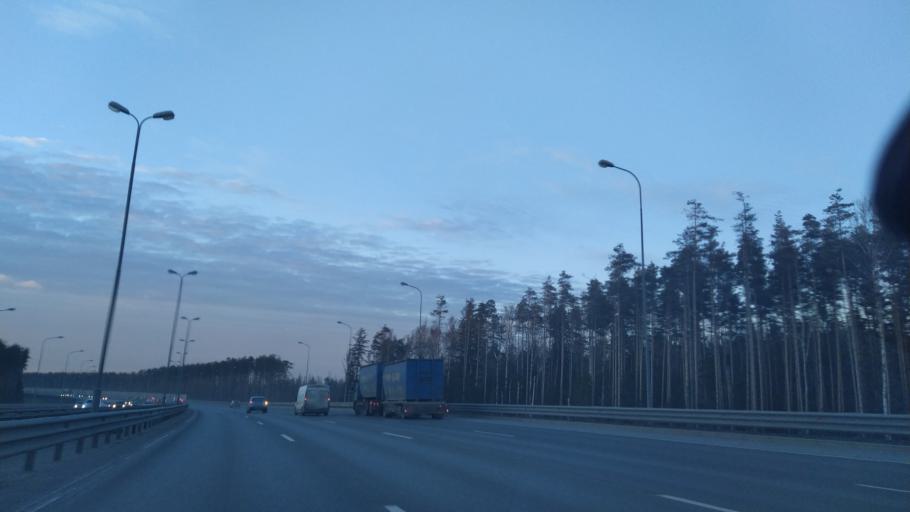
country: RU
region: Leningrad
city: Yanino Vtoroye
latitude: 59.9663
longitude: 30.5531
